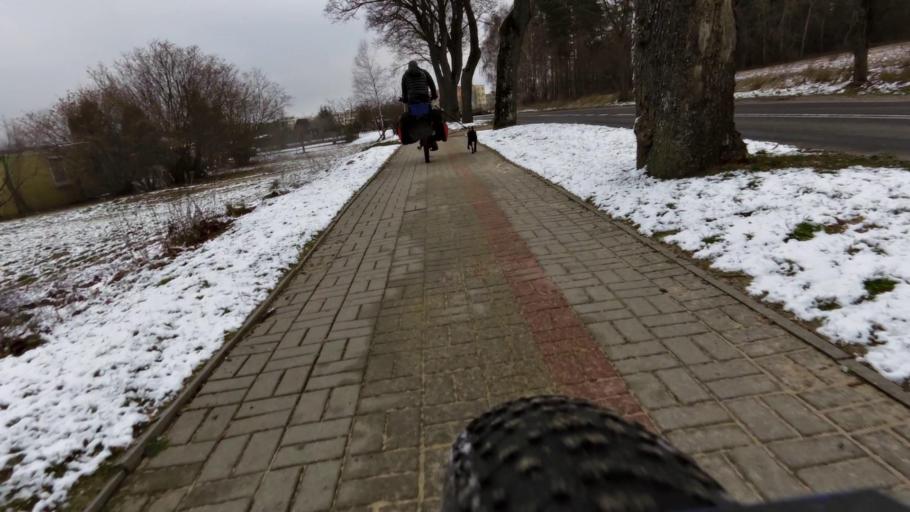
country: PL
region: West Pomeranian Voivodeship
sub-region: Powiat walecki
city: Miroslawiec
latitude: 53.3682
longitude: 16.0845
